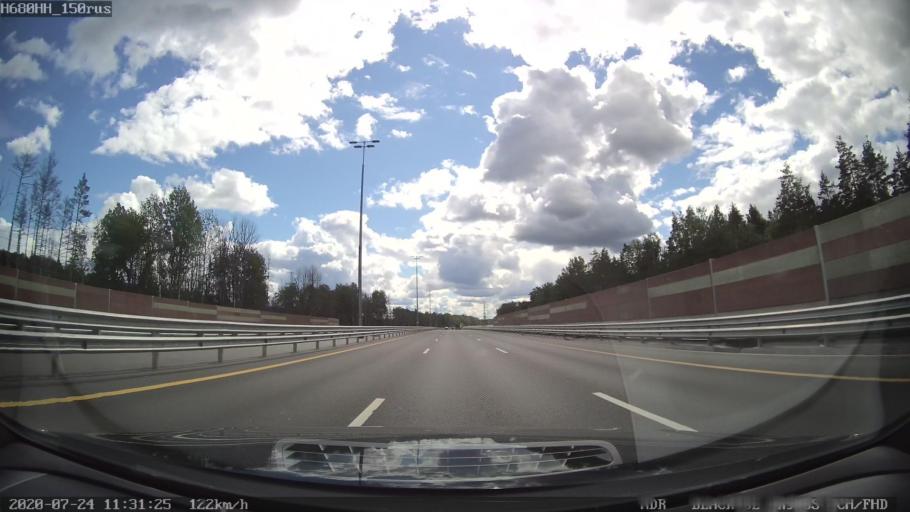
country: RU
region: Leningrad
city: Krasnyy Bor
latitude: 59.6561
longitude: 30.6371
